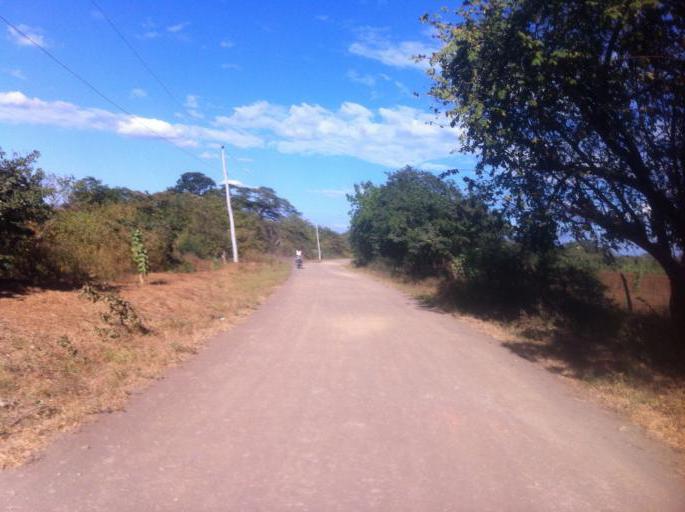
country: NI
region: Managua
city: Carlos Fonseca Amador
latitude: 11.9140
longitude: -86.6053
